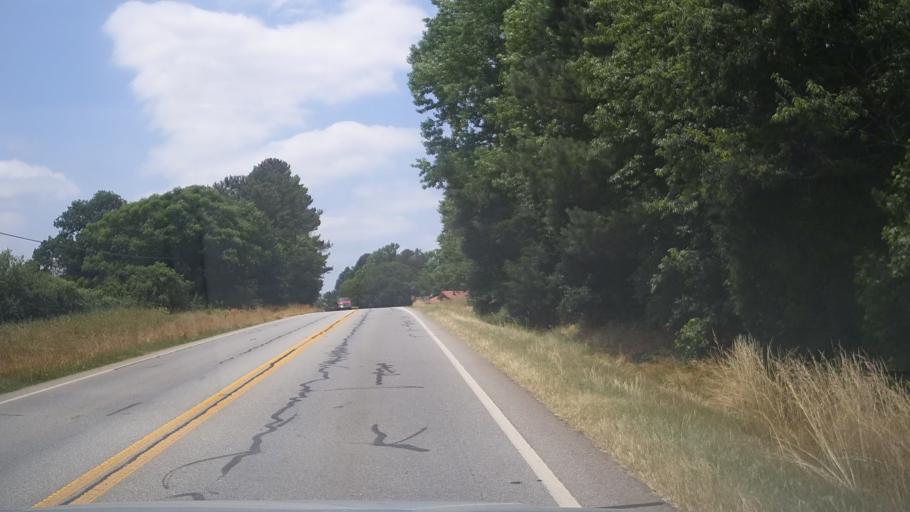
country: US
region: Georgia
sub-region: Jackson County
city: Commerce
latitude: 34.1937
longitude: -83.4163
